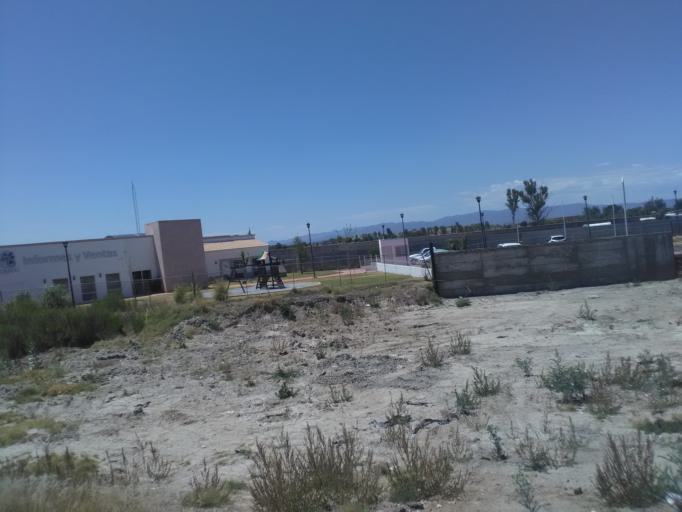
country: MX
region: Durango
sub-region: Durango
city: Jose Refugio Salcido
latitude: 24.0231
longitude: -104.5452
